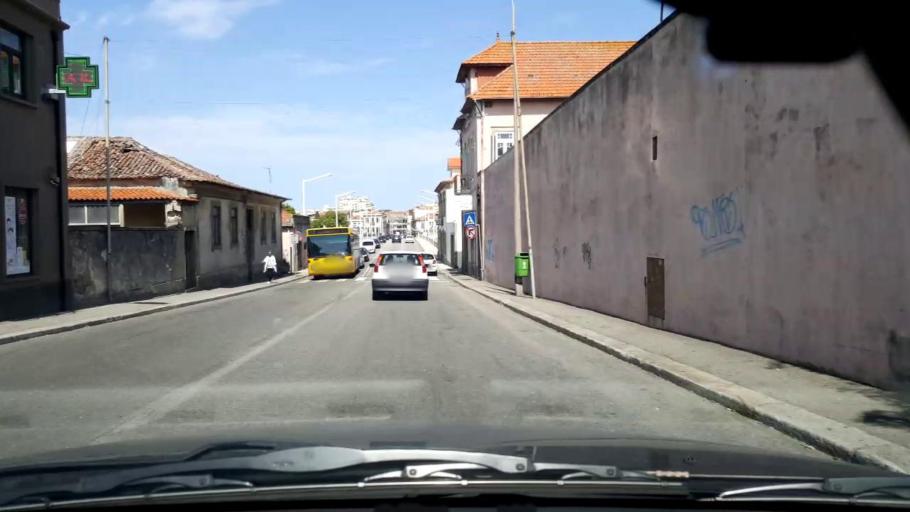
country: PT
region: Porto
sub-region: Vila do Conde
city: Vila do Conde
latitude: 41.3500
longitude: -8.7387
